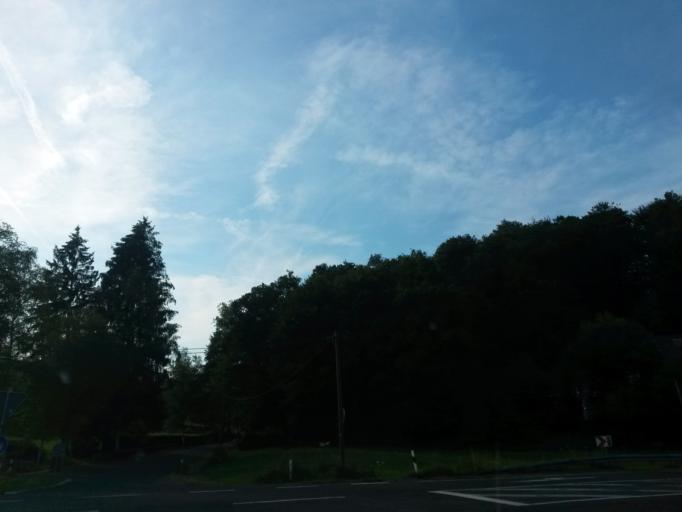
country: DE
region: North Rhine-Westphalia
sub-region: Regierungsbezirk Koln
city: Overath
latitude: 50.9841
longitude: 7.3018
